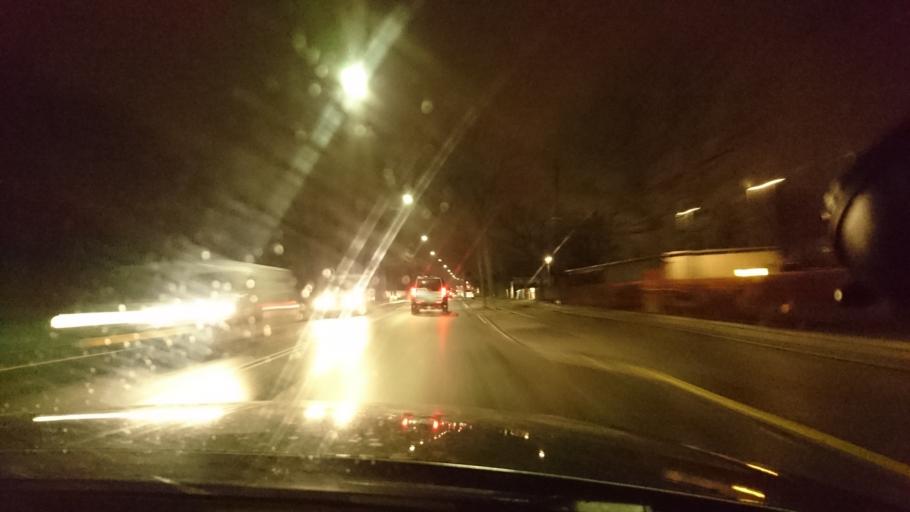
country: DK
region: Capital Region
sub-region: Tarnby Kommune
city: Tarnby
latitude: 55.6489
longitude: 12.5921
